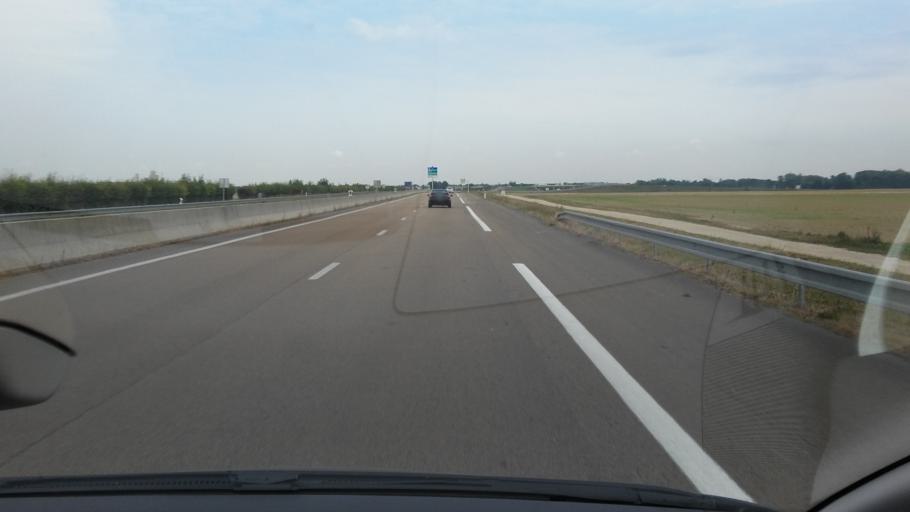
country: FR
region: Champagne-Ardenne
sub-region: Departement de la Marne
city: Connantre
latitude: 48.7419
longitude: 3.9556
